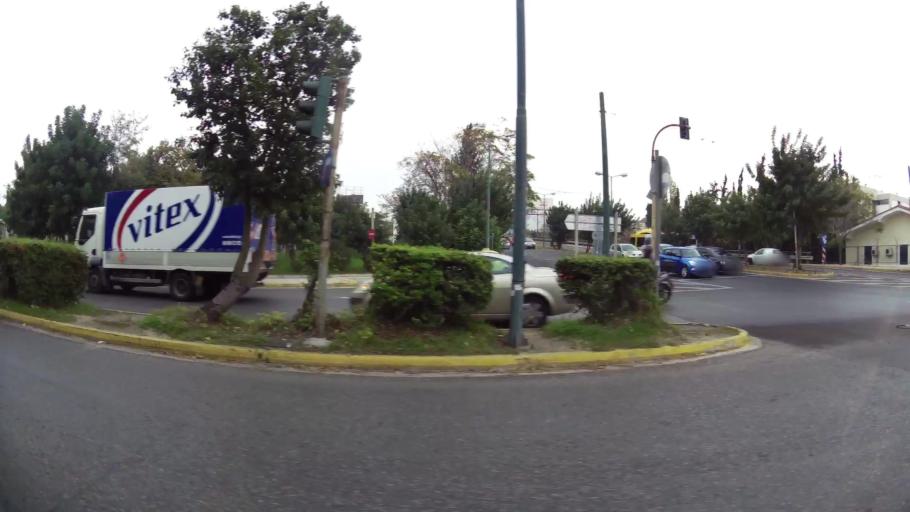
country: GR
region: Attica
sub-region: Nomarchia Athinas
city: Tavros
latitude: 37.9755
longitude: 23.7028
